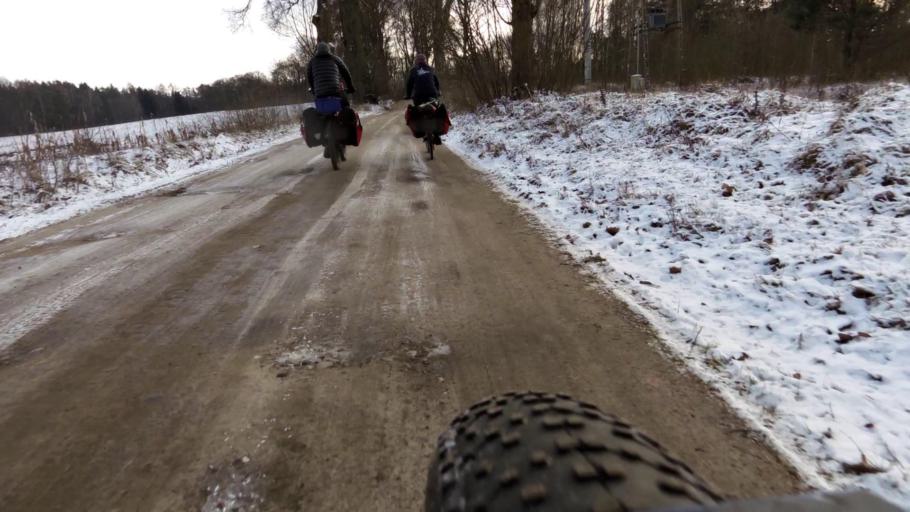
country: PL
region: West Pomeranian Voivodeship
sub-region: Powiat walecki
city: Walcz
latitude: 53.2658
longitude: 16.3119
